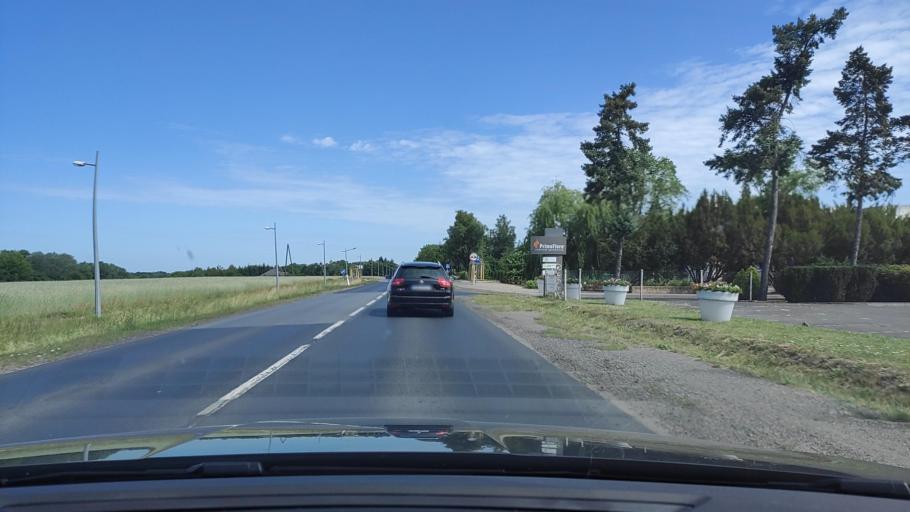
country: PL
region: Greater Poland Voivodeship
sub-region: Powiat poznanski
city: Czerwonak
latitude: 52.5020
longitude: 16.9761
